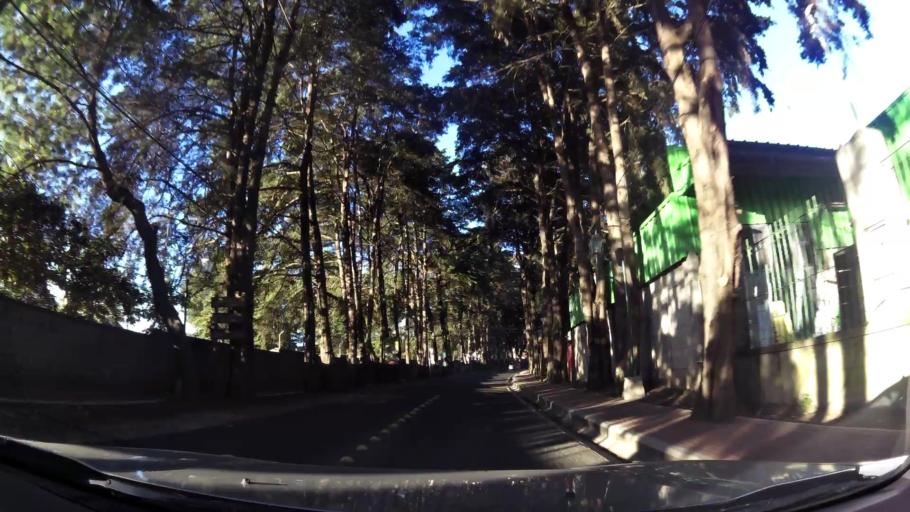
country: GT
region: Sacatepequez
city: San Lucas Sacatepequez
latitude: 14.6106
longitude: -90.6644
